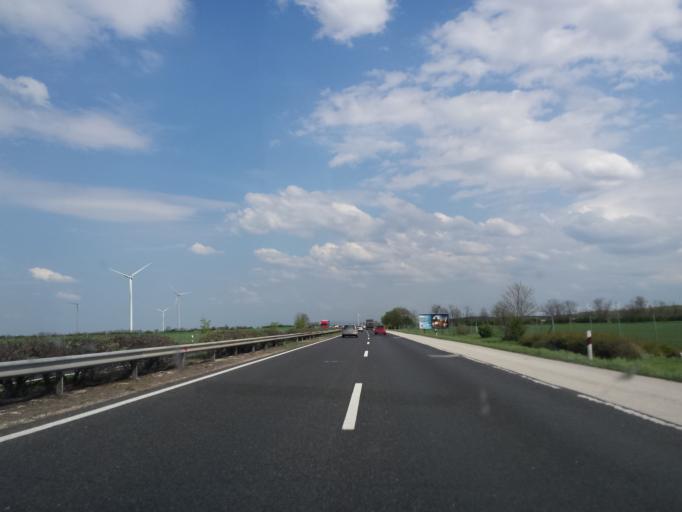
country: HU
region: Komarom-Esztergom
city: Babolna
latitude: 47.6791
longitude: 17.9313
